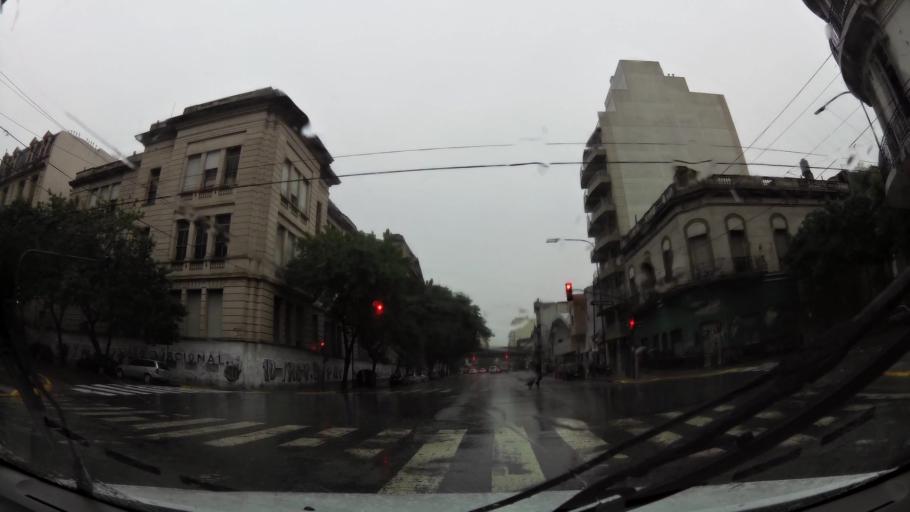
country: AR
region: Buenos Aires F.D.
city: Buenos Aires
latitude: -34.6253
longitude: -58.3914
